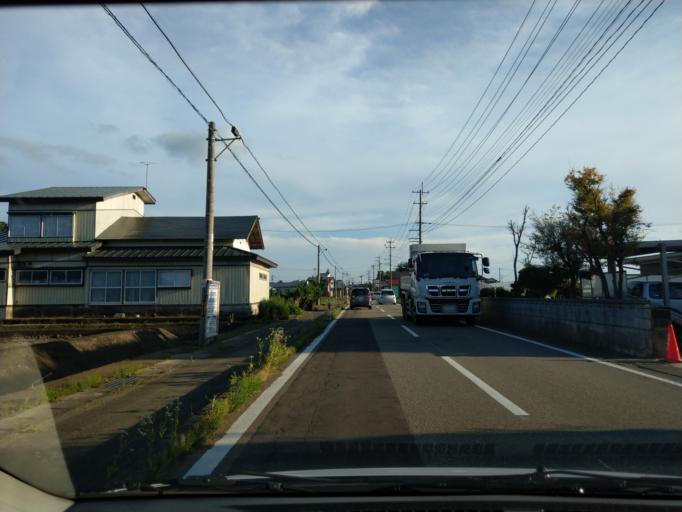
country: JP
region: Akita
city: Omagari
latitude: 39.4453
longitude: 140.5668
